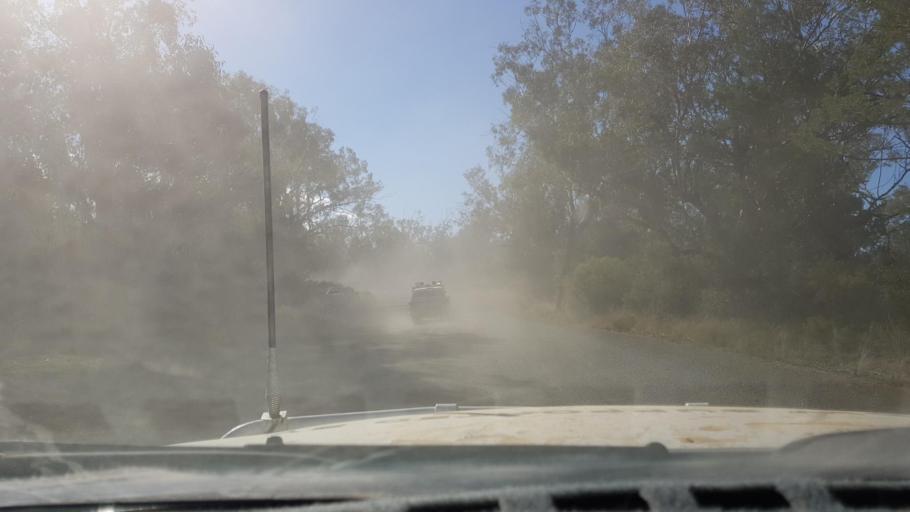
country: AU
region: New South Wales
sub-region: Tamworth Municipality
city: Manilla
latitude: -30.6508
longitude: 150.4946
